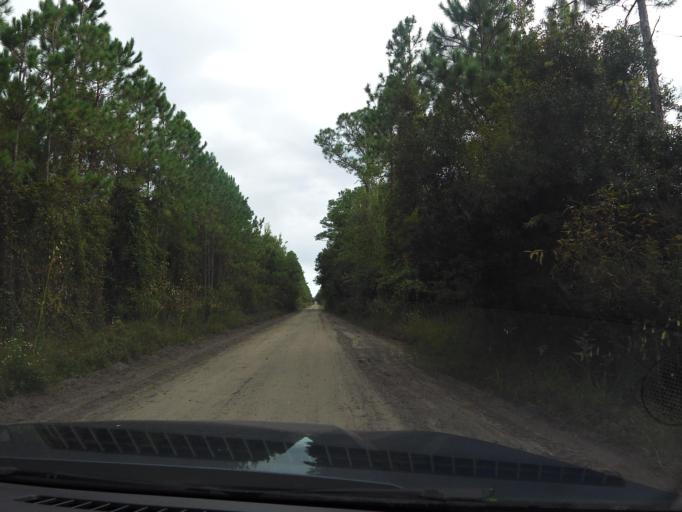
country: US
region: Florida
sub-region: Flagler County
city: Palm Coast
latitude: 29.5775
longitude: -81.3417
